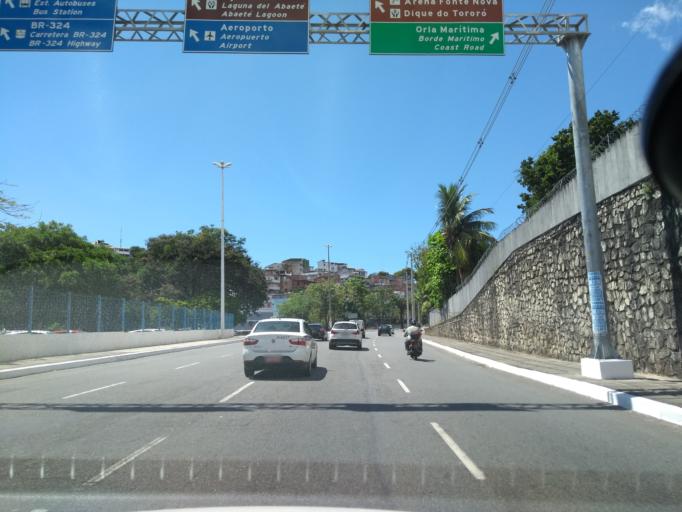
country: BR
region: Bahia
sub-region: Salvador
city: Salvador
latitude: -12.9899
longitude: -38.5122
